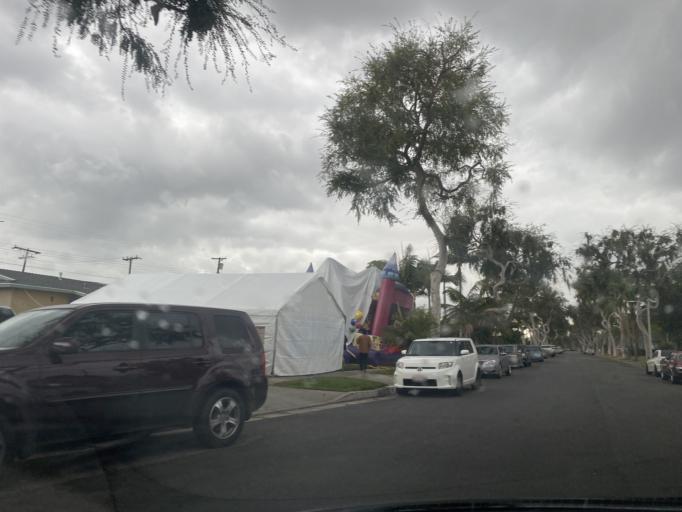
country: US
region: California
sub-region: Orange County
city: Fullerton
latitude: 33.8636
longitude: -117.9151
